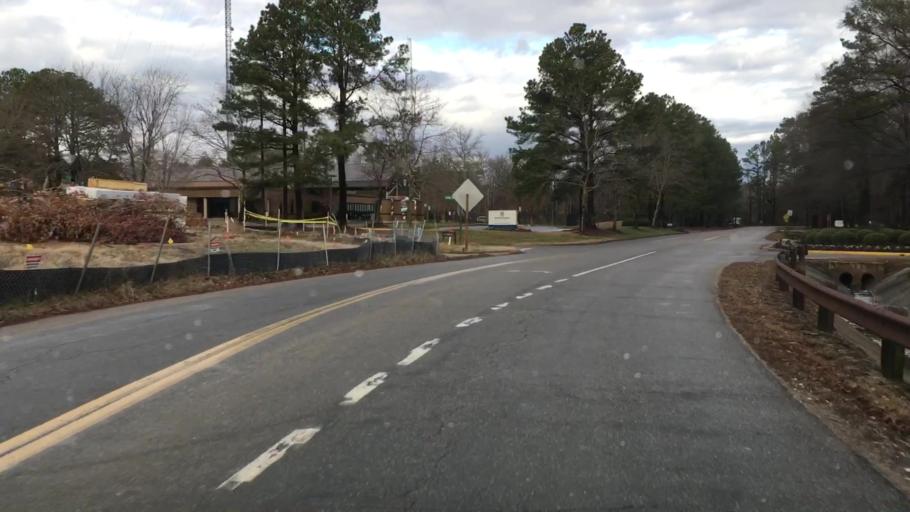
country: US
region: Virginia
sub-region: Chesterfield County
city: Bon Air
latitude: 37.5100
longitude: -77.5971
